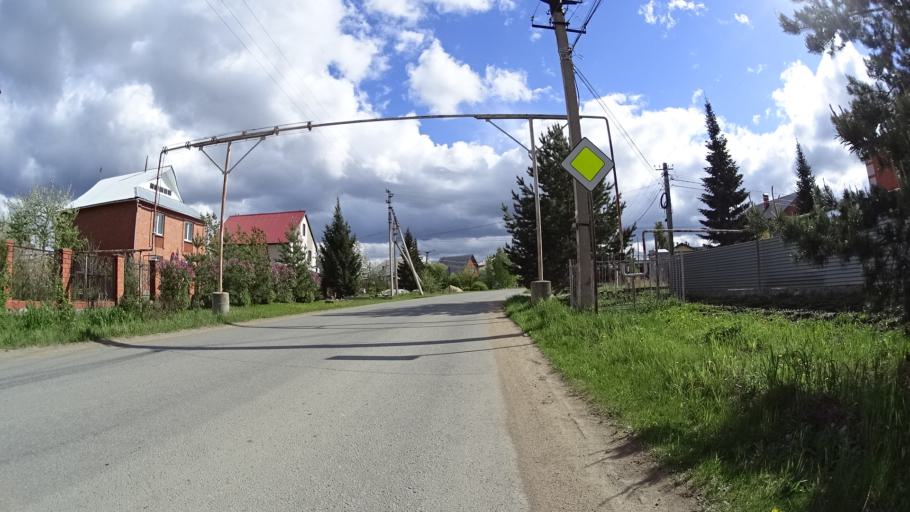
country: RU
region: Chelyabinsk
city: Sargazy
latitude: 55.1484
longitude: 61.2375
